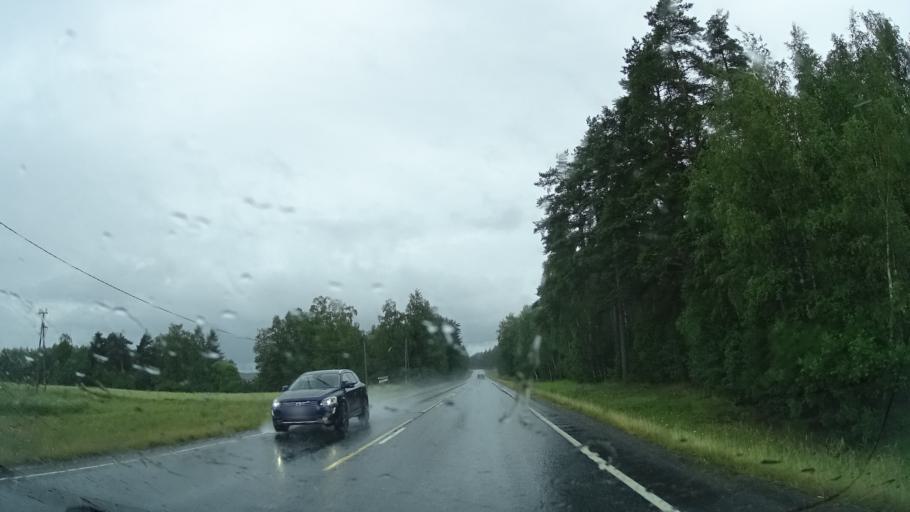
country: FI
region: Haeme
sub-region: Forssa
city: Humppila
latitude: 60.9696
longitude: 23.2794
